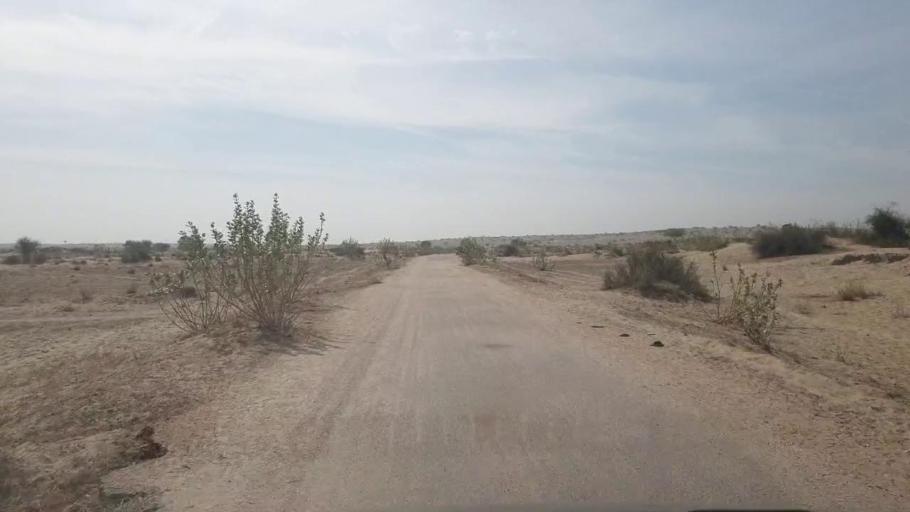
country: PK
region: Sindh
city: Umarkot
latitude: 25.2866
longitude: 69.7286
